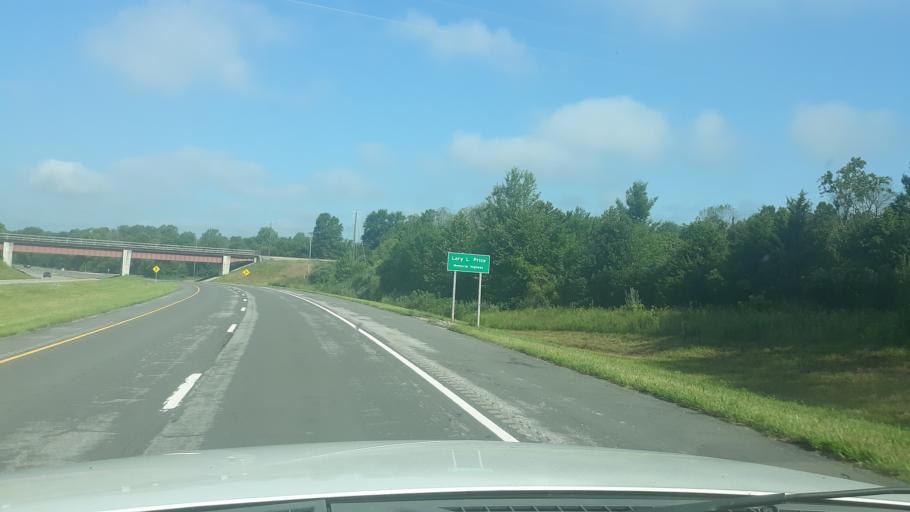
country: US
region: Illinois
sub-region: Saline County
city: Carrier Mills
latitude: 37.7380
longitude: -88.7079
